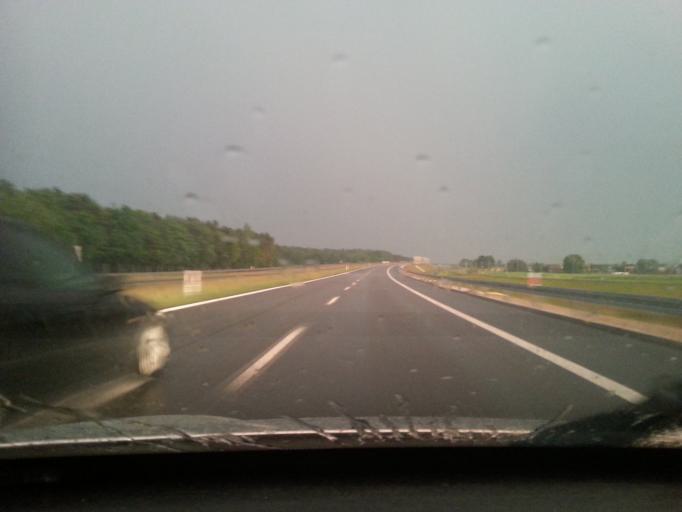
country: PL
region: Lodz Voivodeship
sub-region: Powiat pabianicki
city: Dobron
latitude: 51.6206
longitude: 19.2745
